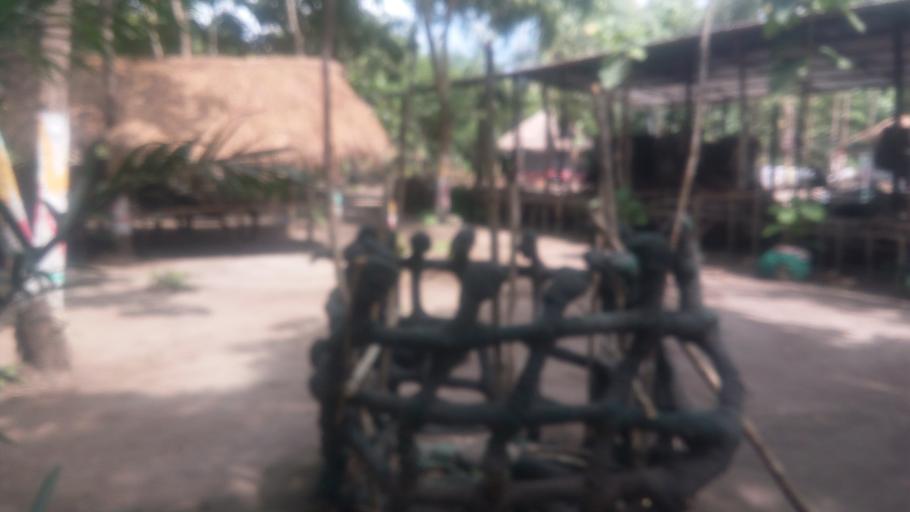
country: TG
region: Maritime
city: Tsevie
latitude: 6.4747
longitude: 1.1889
